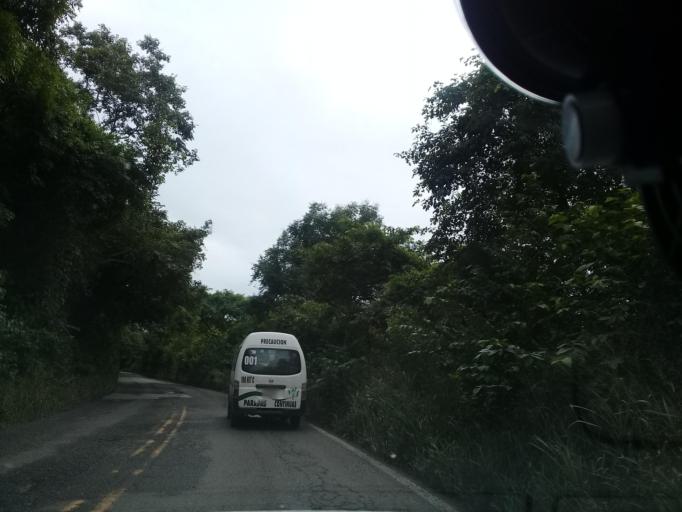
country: MX
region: Veracruz
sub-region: Chalma
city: San Pedro Coyutla
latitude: 21.2035
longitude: -98.3892
